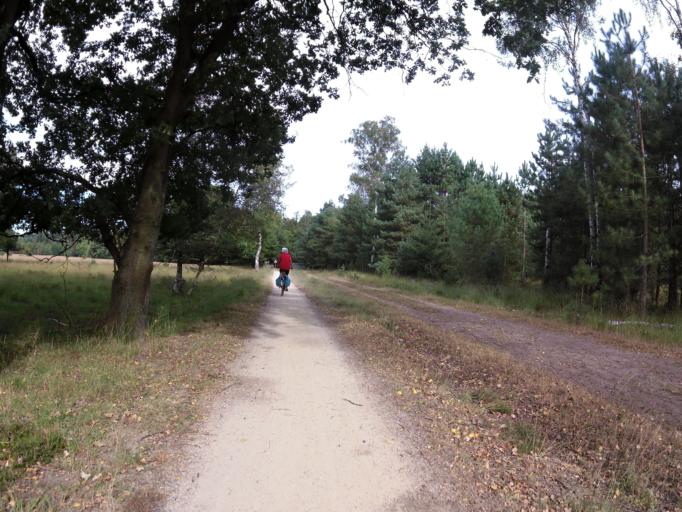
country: NL
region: North Brabant
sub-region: Gemeente Valkenswaard
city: Valkenswaard
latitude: 51.3344
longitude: 5.4950
